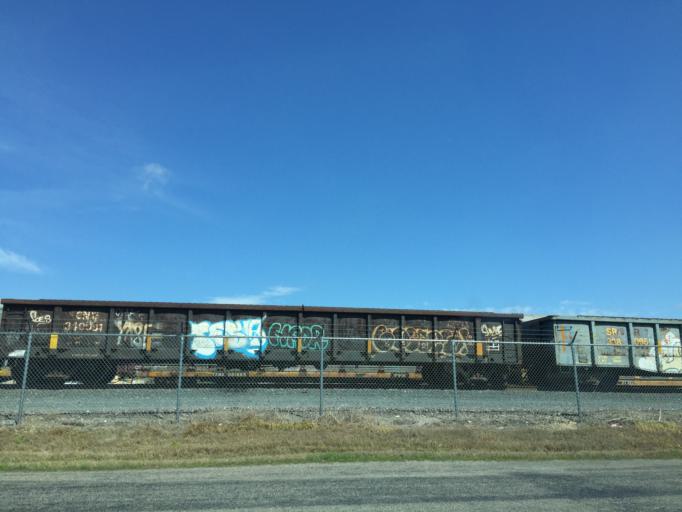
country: US
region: Texas
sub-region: Williamson County
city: Taylor
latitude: 30.5662
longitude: -97.4224
